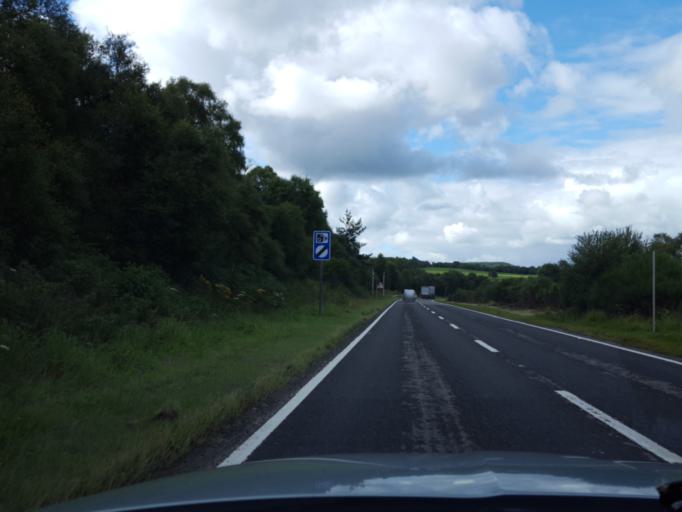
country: GB
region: Scotland
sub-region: Highland
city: Grantown on Spey
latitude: 57.3225
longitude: -3.5583
